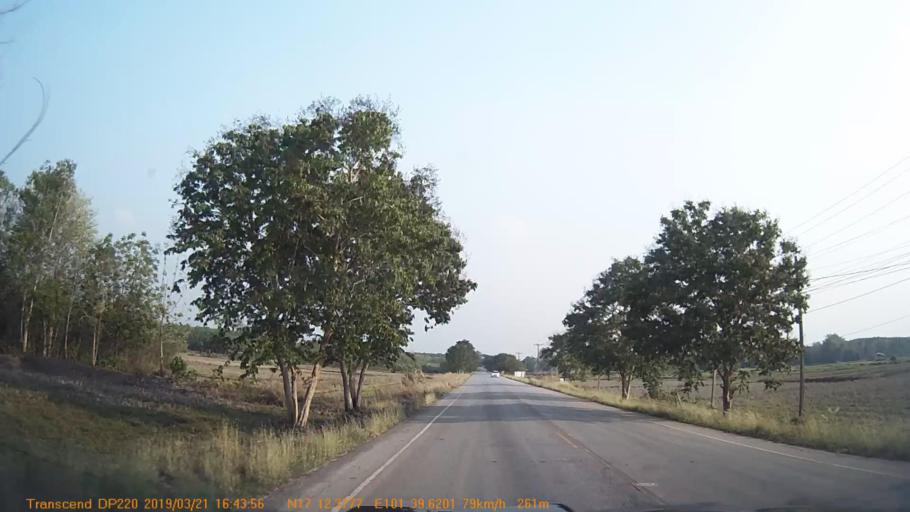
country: TH
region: Loei
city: Phu Luang
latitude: 17.2060
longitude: 101.6604
